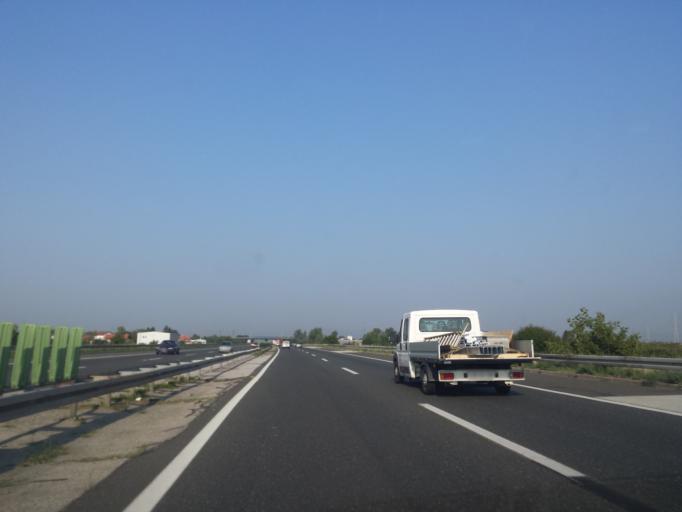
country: HR
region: Grad Zagreb
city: Novi Zagreb
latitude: 45.7531
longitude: 15.9727
